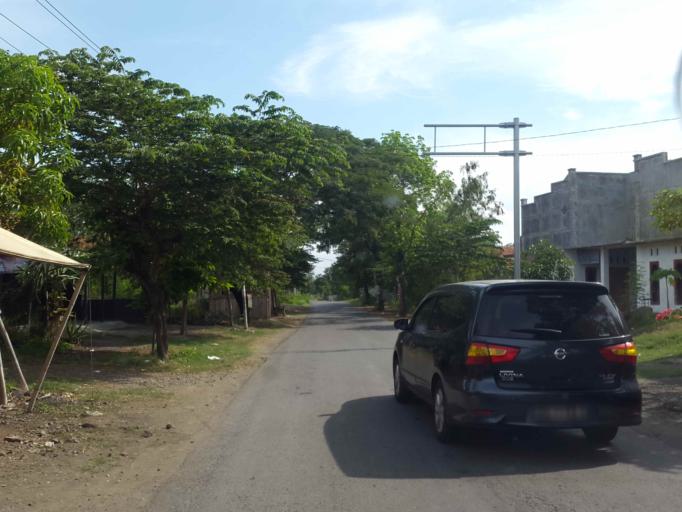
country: ID
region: Central Java
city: Pemalang
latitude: -6.8709
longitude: 109.3288
